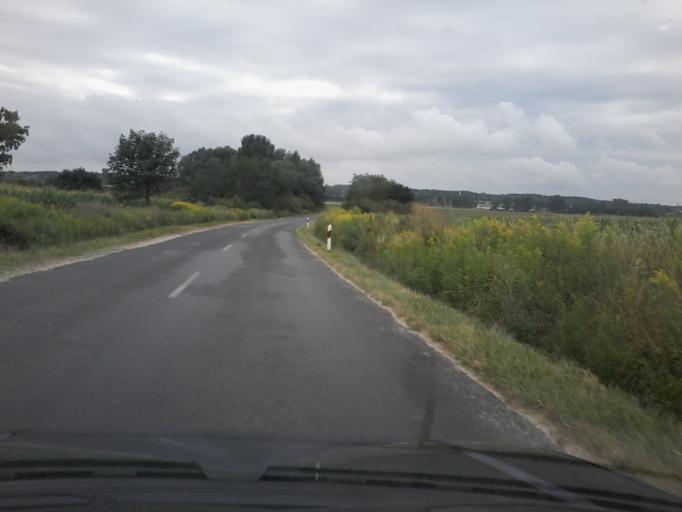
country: HU
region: Vas
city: Sarvar
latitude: 47.2073
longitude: 17.0428
